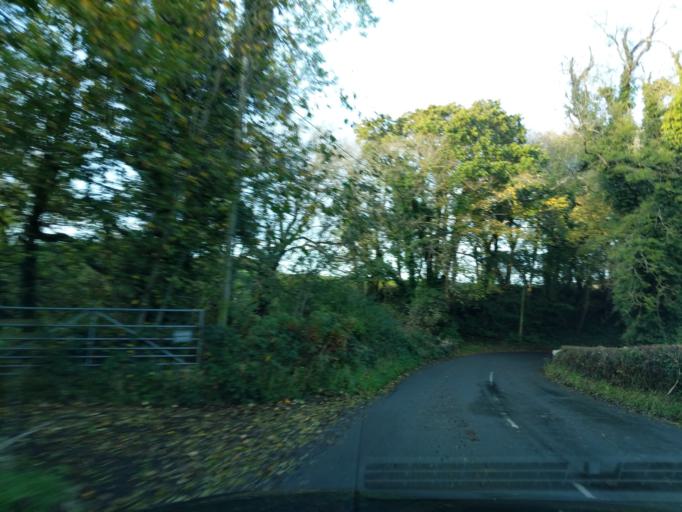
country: GB
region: Scotland
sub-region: Dumfries and Galloway
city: Kirkcudbright
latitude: 54.8123
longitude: -4.0956
